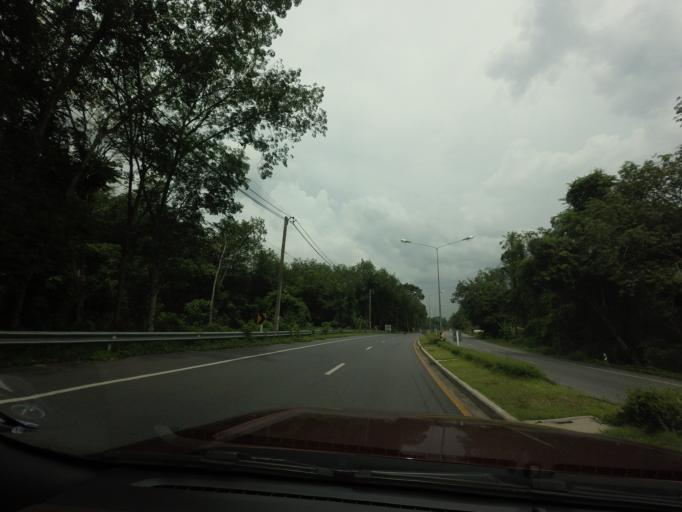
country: TH
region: Yala
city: Krong Pi Nang
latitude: 6.4652
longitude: 101.2720
